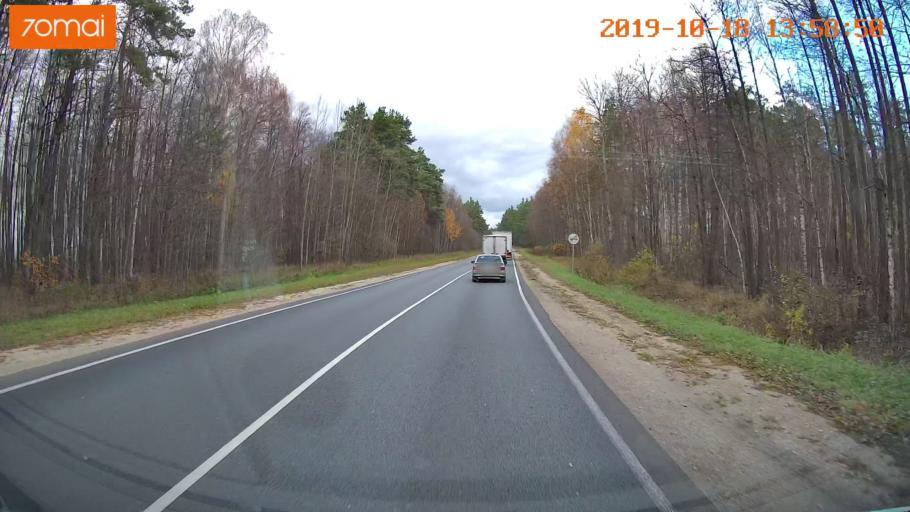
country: RU
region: Rjazan
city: Spas-Klepiki
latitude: 55.0888
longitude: 40.0573
